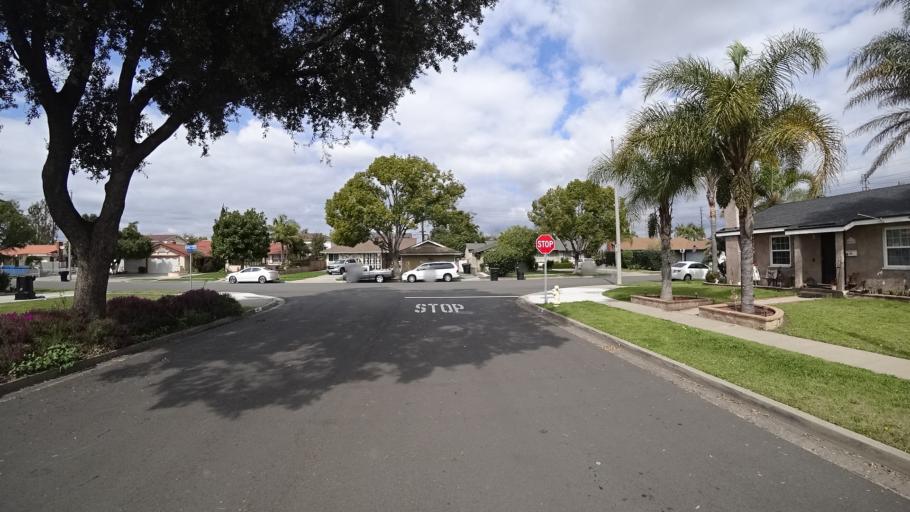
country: US
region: California
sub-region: Orange County
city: Buena Park
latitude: 33.8377
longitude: -117.9826
